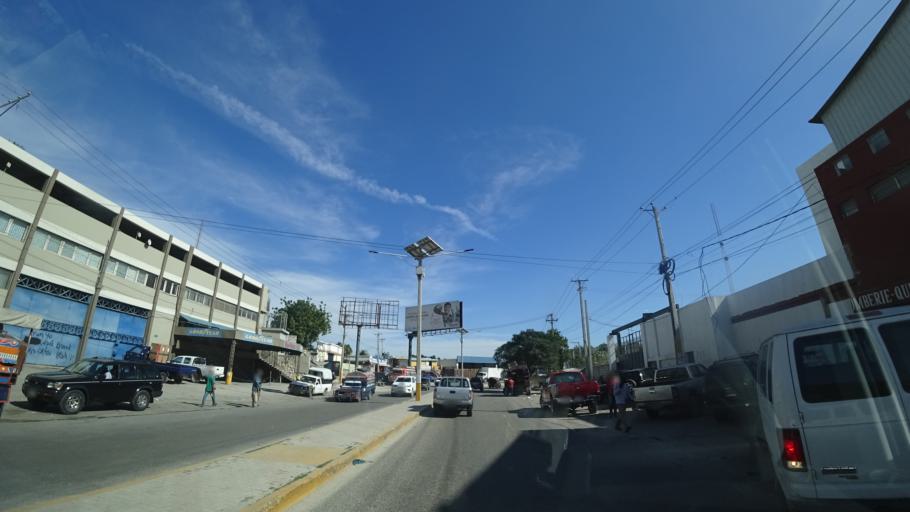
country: HT
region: Ouest
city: Delmas 73
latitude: 18.5563
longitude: -72.3154
